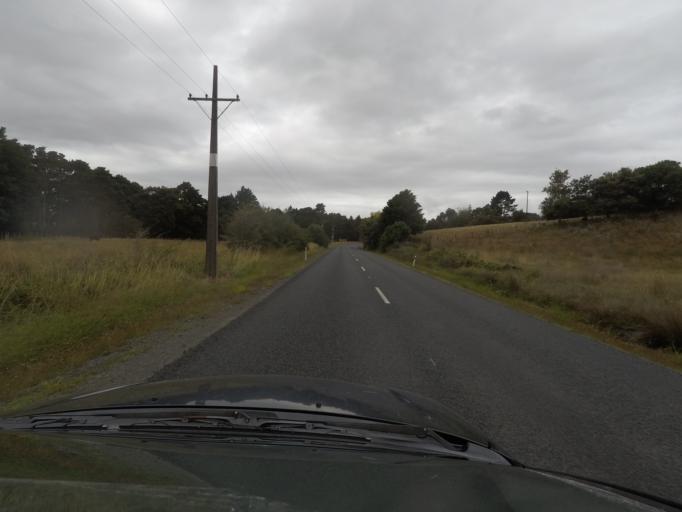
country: NZ
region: Auckland
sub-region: Auckland
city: Wellsford
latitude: -36.2796
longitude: 174.5806
